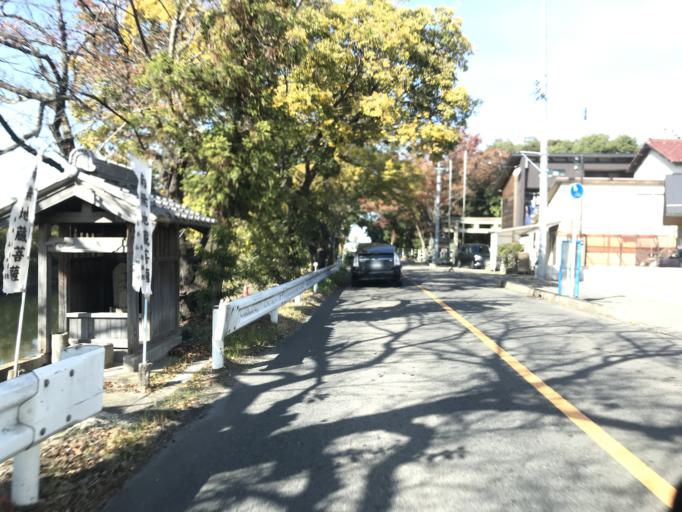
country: JP
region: Aichi
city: Iwakura
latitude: 35.2313
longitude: 136.8452
